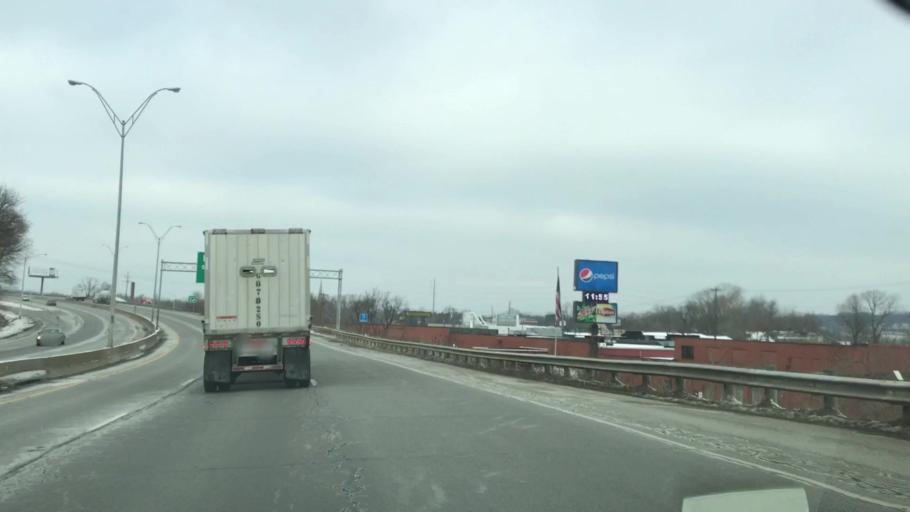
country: US
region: Ohio
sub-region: Mahoning County
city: Youngstown
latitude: 41.0994
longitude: -80.6596
